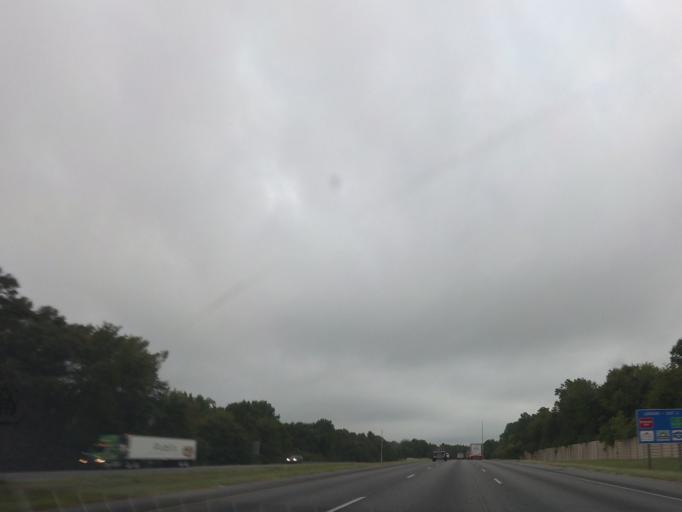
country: US
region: Georgia
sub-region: Bibb County
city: West Point
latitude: 32.7829
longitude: -83.7168
